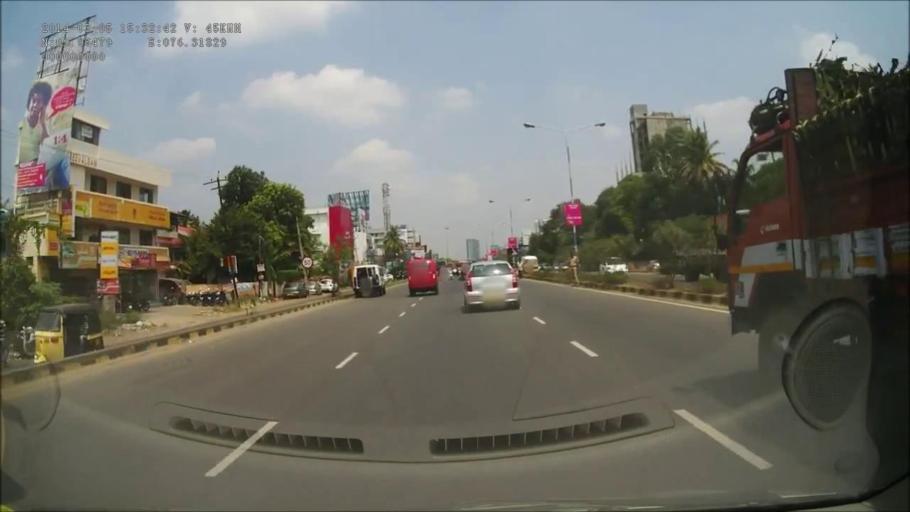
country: IN
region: Kerala
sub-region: Ernakulam
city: Cochin
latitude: 9.9646
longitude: 76.3183
